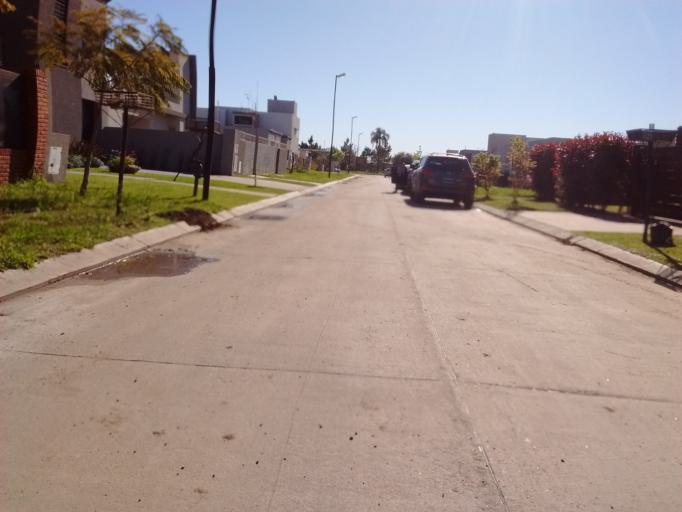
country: AR
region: Santa Fe
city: Funes
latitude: -32.9251
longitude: -60.8468
